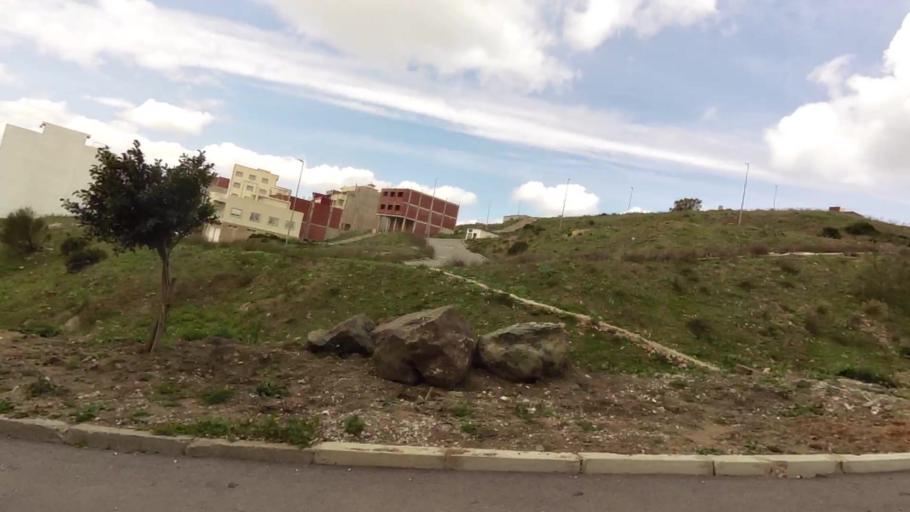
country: MA
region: Tanger-Tetouan
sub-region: Tanger-Assilah
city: Tangier
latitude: 35.7690
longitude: -5.7506
